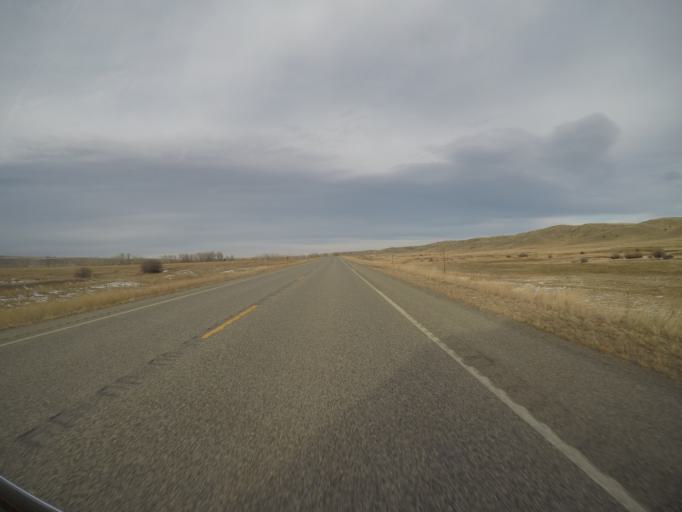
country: US
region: Montana
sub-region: Stillwater County
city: Absarokee
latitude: 45.4452
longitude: -109.4478
